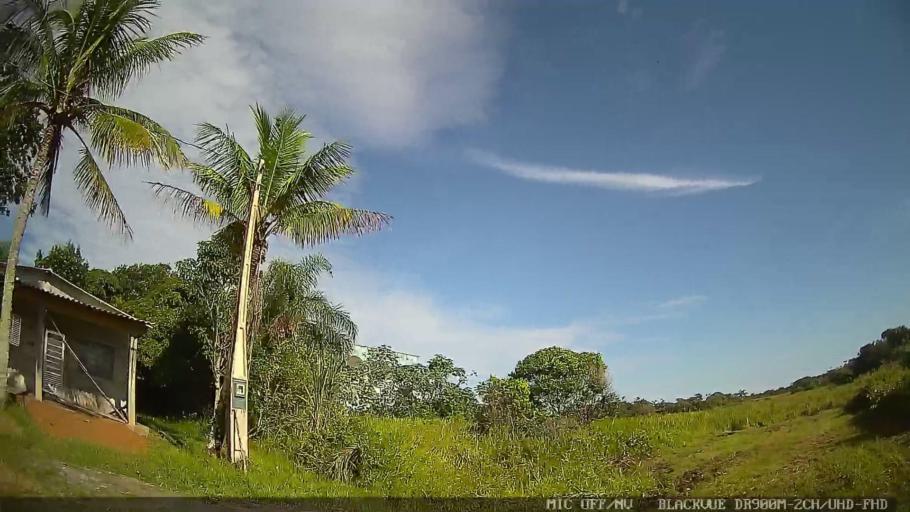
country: BR
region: Sao Paulo
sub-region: Iguape
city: Iguape
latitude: -24.7628
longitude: -47.5822
